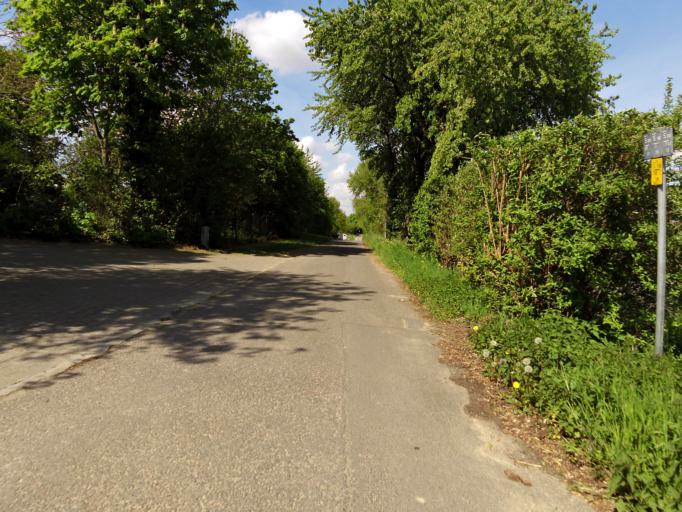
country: DE
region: Rheinland-Pfalz
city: Bechtheim
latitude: 49.7033
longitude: 8.2979
